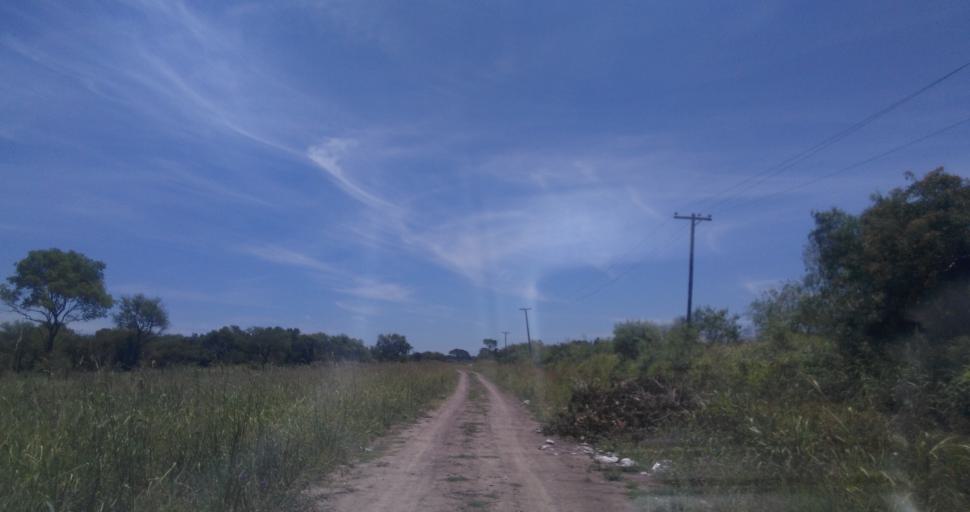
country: AR
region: Chaco
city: Fontana
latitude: -27.4326
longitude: -59.0398
